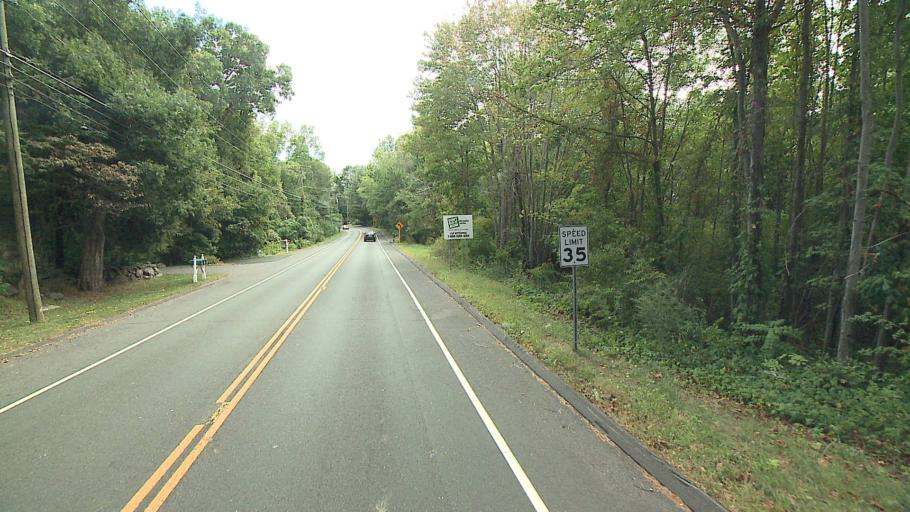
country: US
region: Connecticut
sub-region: Fairfield County
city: Westport
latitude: 41.1704
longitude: -73.3871
